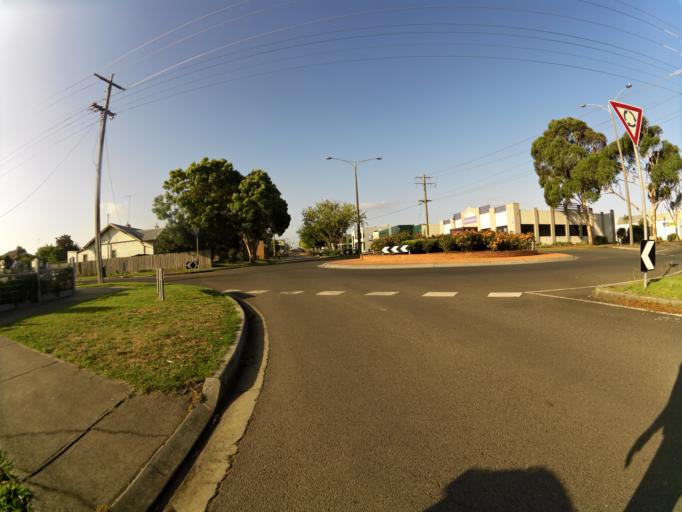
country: AU
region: Victoria
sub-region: Latrobe
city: Morwell
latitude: -38.2395
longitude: 146.3941
